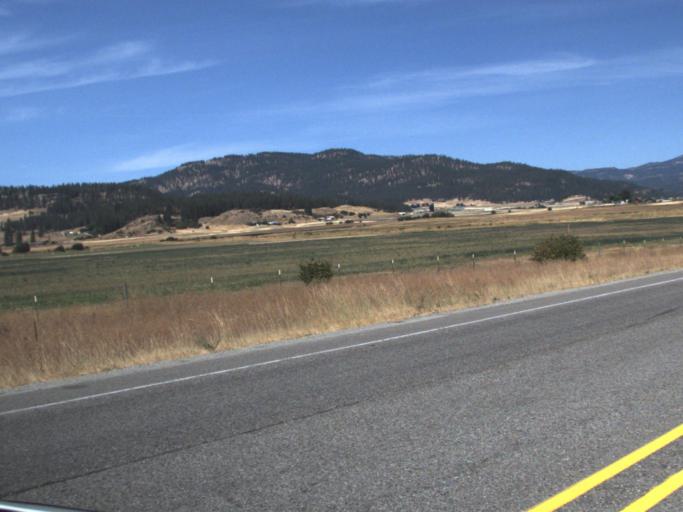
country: US
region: Washington
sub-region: Stevens County
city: Chewelah
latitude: 48.2115
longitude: -117.7153
